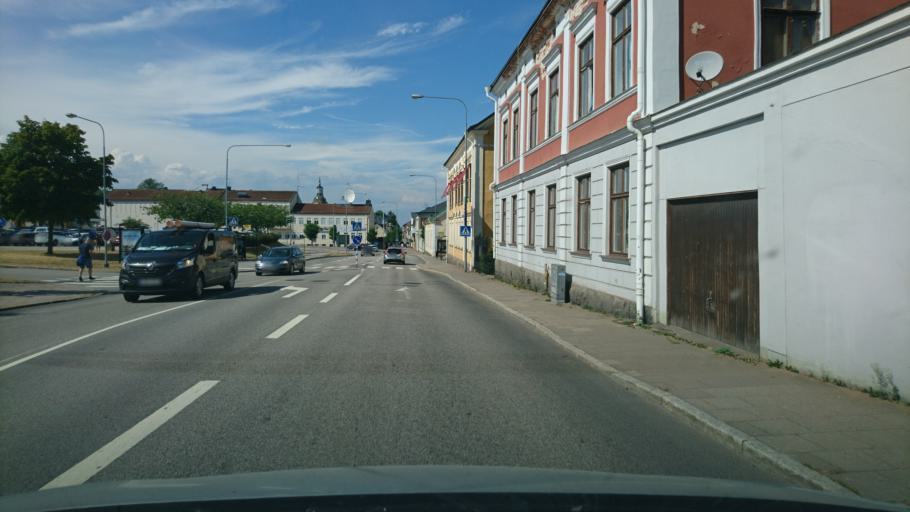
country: SE
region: Kalmar
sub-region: Vasterviks Kommun
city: Vaestervik
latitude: 57.7563
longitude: 16.6378
